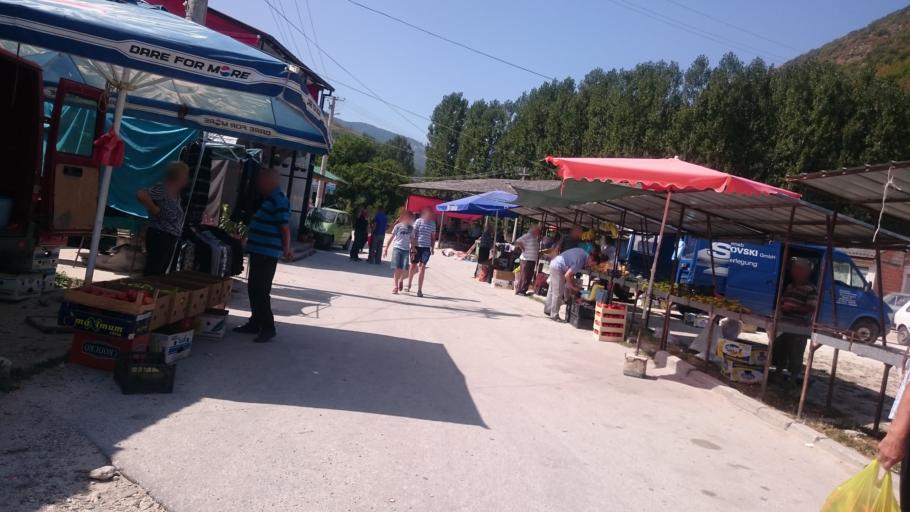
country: MK
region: Makedonski Brod
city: Makedonski Brod
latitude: 41.5069
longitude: 21.2165
